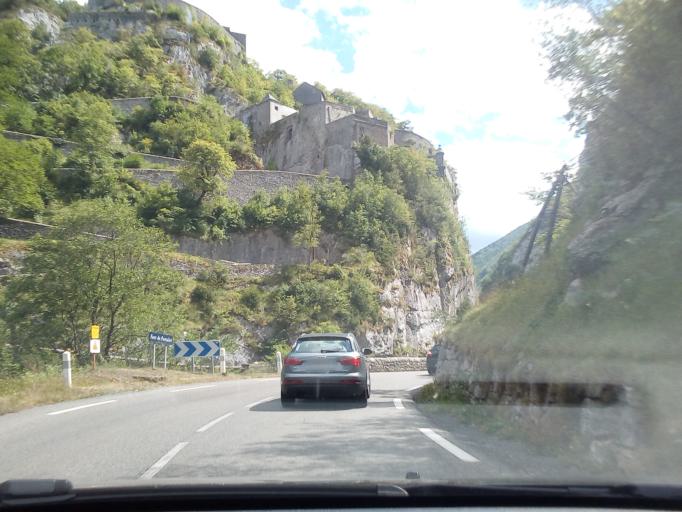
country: FR
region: Aquitaine
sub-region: Departement des Pyrenees-Atlantiques
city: Laruns
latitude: 42.8877
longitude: -0.5630
